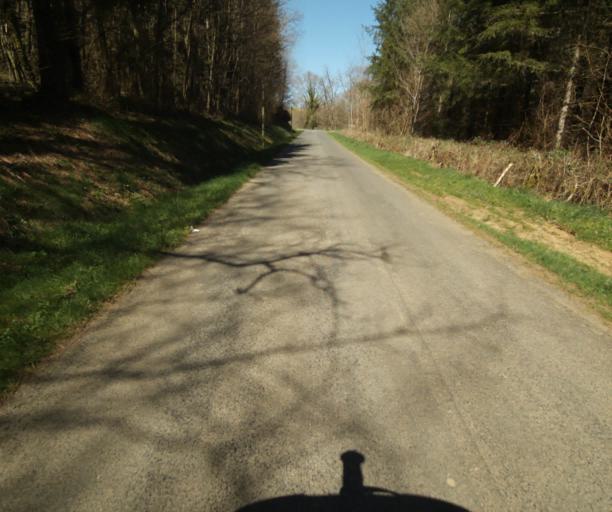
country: FR
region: Limousin
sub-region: Departement de la Correze
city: Chamboulive
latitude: 45.4573
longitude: 1.6733
